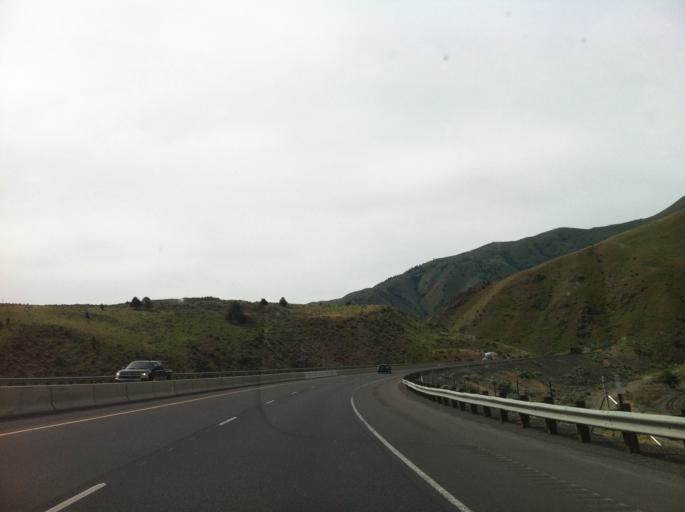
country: US
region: Idaho
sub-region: Washington County
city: Weiser
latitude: 44.5169
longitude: -117.3750
